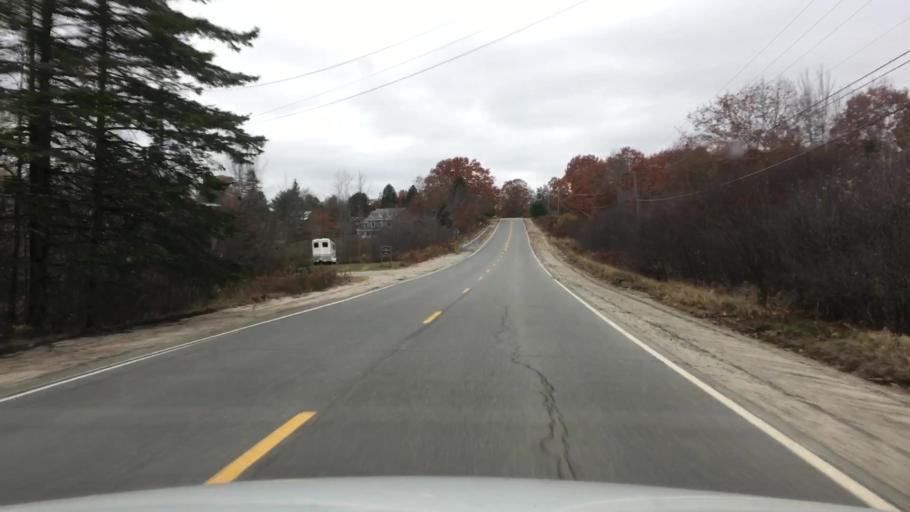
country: US
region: Maine
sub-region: Hancock County
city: Sedgwick
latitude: 44.3890
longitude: -68.5780
